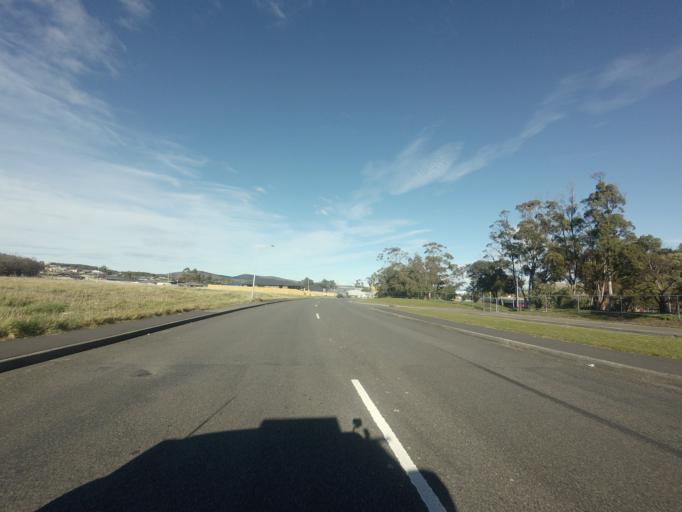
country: AU
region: Tasmania
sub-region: Clarence
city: Rokeby
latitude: -42.8966
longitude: 147.4469
